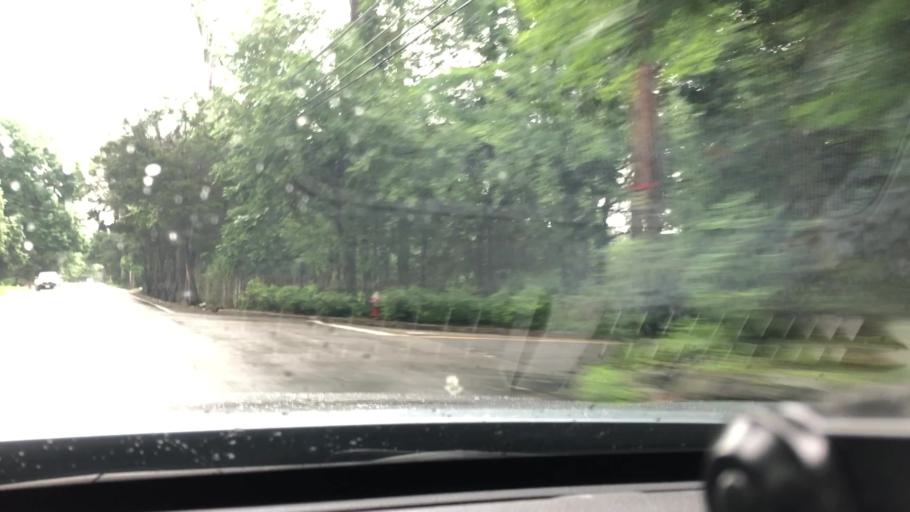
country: US
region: New Jersey
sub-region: Bergen County
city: Woodcliff Lake
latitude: 41.0362
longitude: -74.0816
